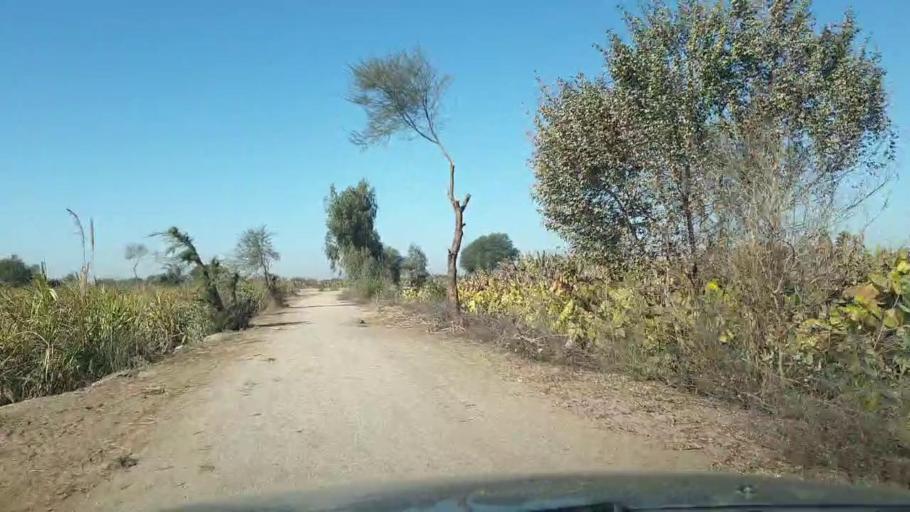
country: PK
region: Sindh
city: Ghotki
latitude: 28.0173
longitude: 69.2702
